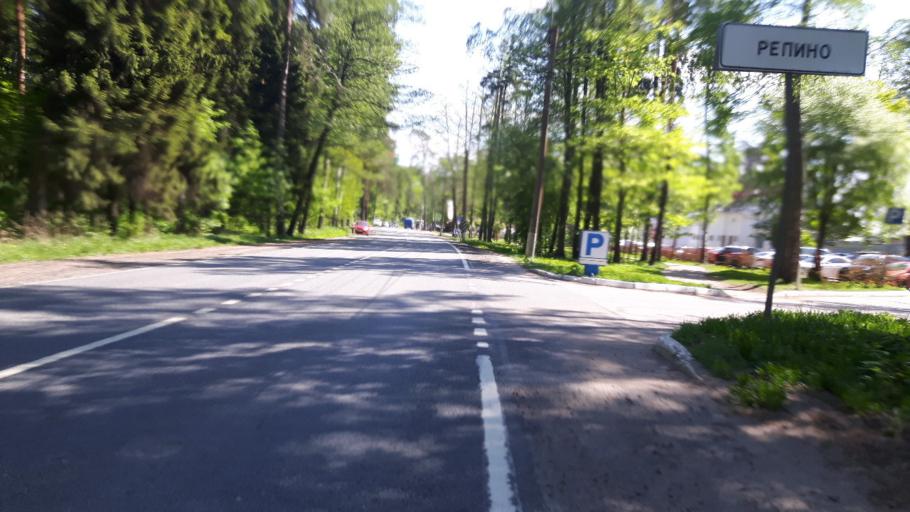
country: RU
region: St.-Petersburg
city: Komarovo
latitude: 60.1687
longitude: 29.8205
